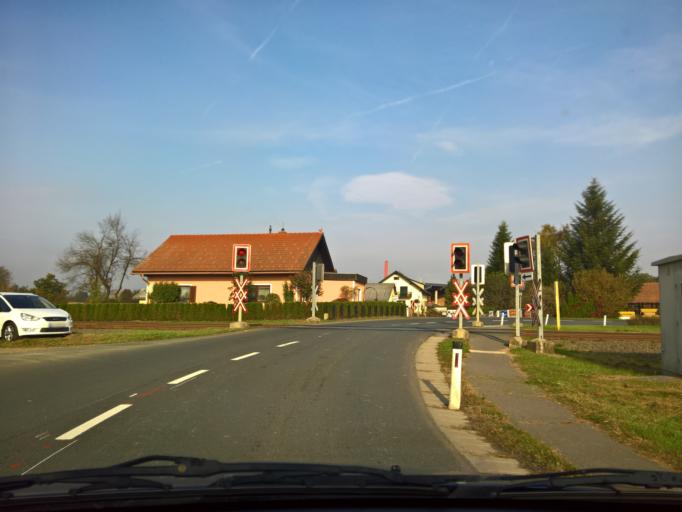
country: AT
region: Styria
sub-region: Politischer Bezirk Deutschlandsberg
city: Gross Sankt Florian
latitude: 46.8199
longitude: 15.3152
